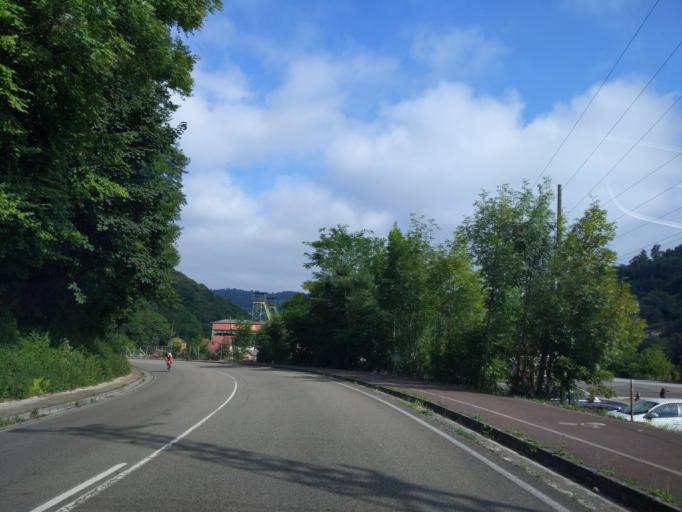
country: ES
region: Asturias
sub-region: Province of Asturias
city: El entrego
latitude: 43.2785
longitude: -5.6191
